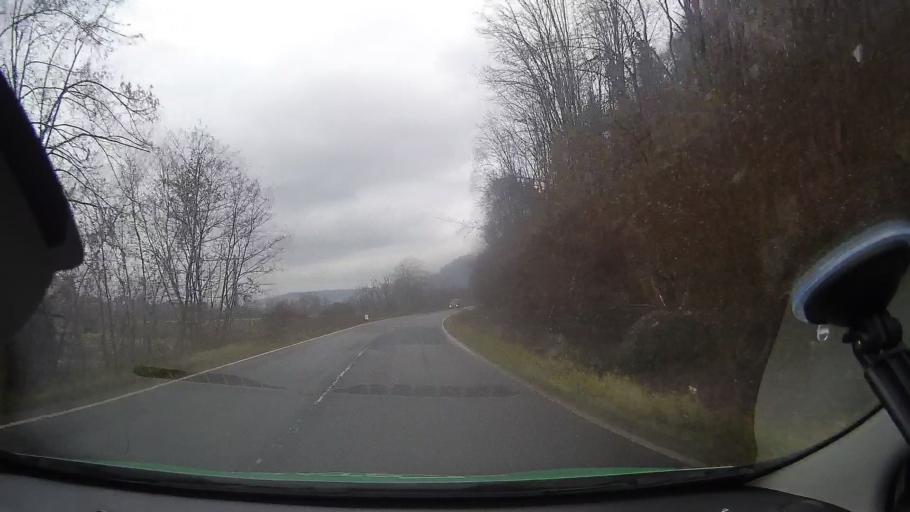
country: RO
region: Arad
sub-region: Comuna Buteni
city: Buteni
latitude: 46.3034
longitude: 22.1587
